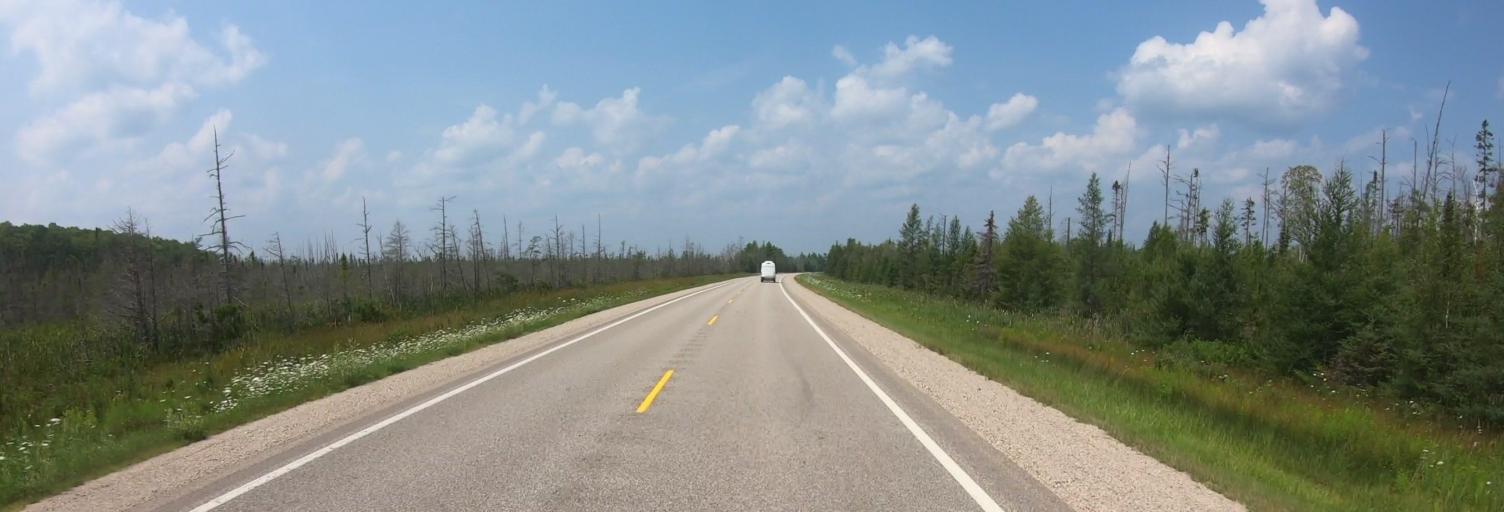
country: US
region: Michigan
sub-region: Luce County
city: Newberry
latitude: 46.3374
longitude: -85.8686
